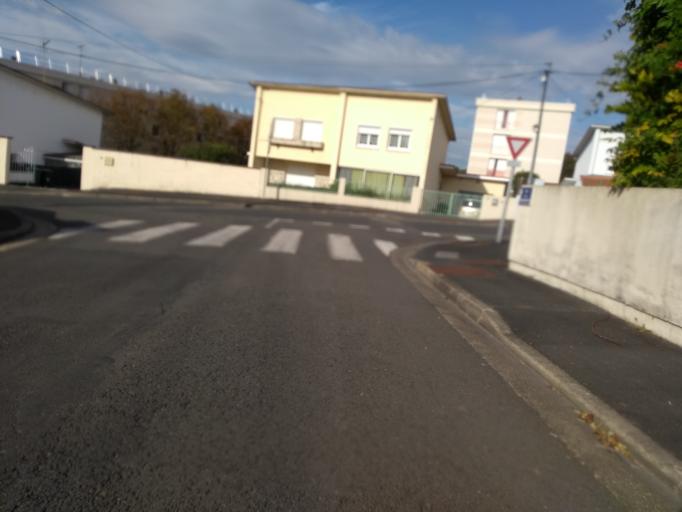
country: FR
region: Aquitaine
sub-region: Departement de la Gironde
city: Gradignan
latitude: 44.7812
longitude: -0.6096
